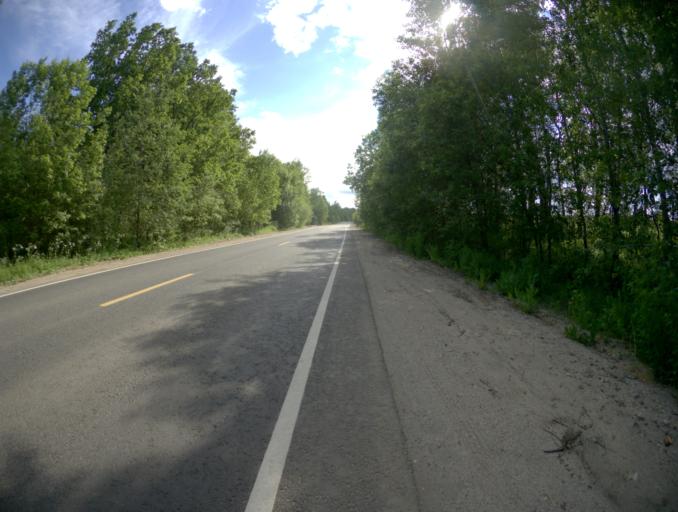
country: RU
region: Ivanovo
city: Kitovo
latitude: 56.8281
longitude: 41.2949
